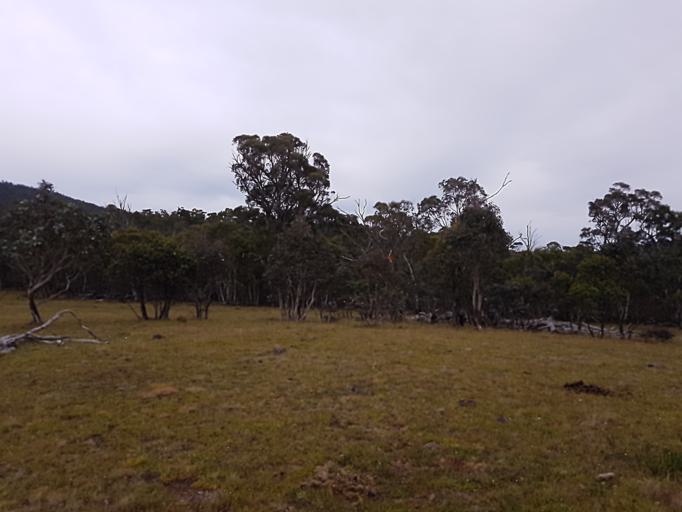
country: AU
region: New South Wales
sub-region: Snowy River
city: Jindabyne
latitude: -36.7943
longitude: 148.1700
